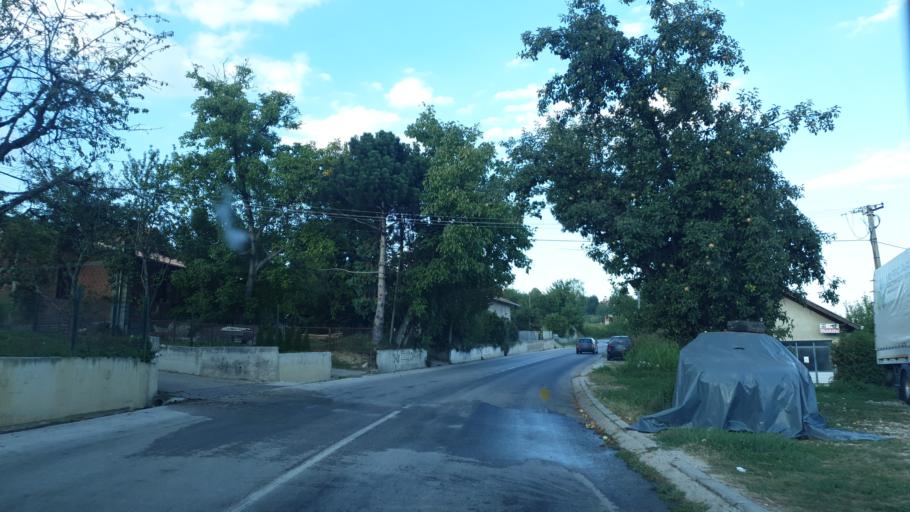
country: RS
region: Central Serbia
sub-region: Zlatiborski Okrug
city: Uzice
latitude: 43.8595
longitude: 19.8783
